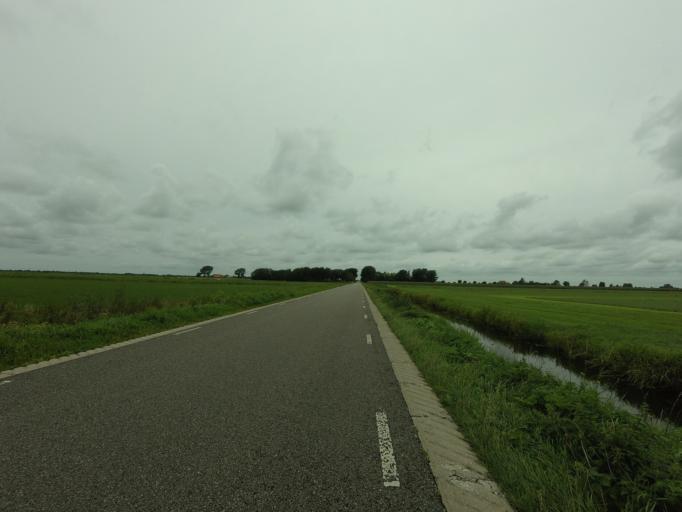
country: NL
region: Overijssel
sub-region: Gemeente Steenwijkerland
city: Oldemarkt
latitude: 52.8098
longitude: 5.9125
